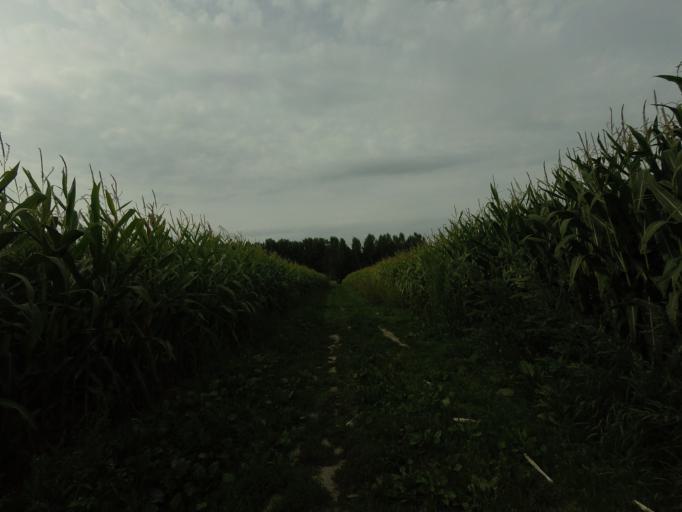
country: BE
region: Flanders
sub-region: Provincie Vlaams-Brabant
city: Kampenhout
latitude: 50.9470
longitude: 4.5443
